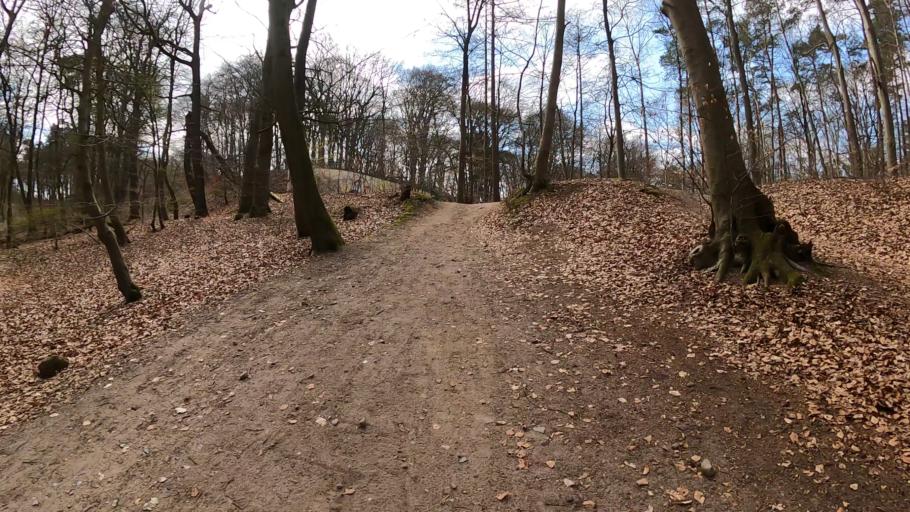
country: DE
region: Hamburg
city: Harburg
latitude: 53.4645
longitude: 9.9342
